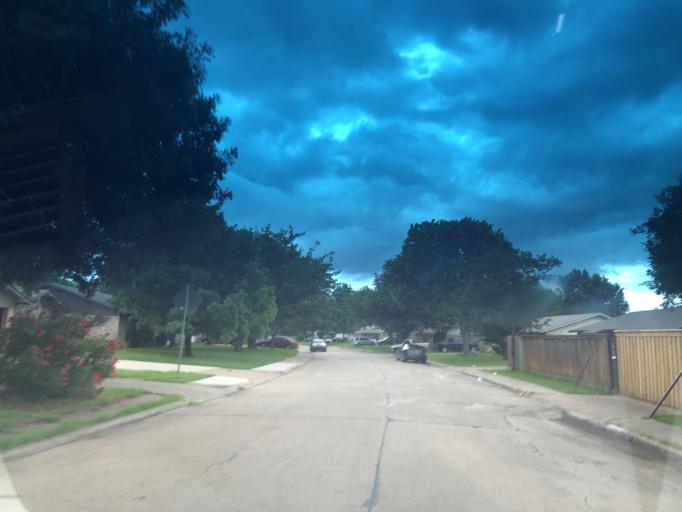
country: US
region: Texas
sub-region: Dallas County
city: Grand Prairie
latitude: 32.7052
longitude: -97.0047
